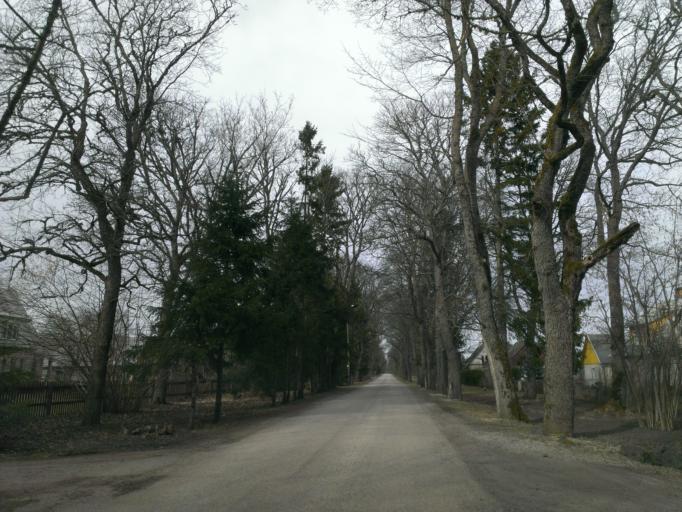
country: EE
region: Laeaene
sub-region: Lihula vald
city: Lihula
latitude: 58.5820
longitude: 23.5372
